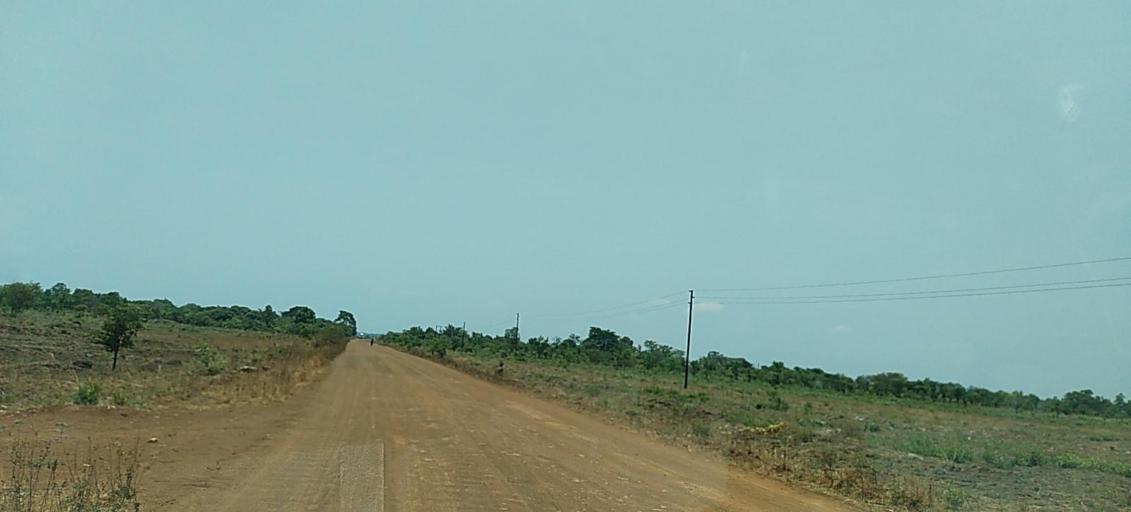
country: ZM
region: Copperbelt
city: Mpongwe
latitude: -13.6796
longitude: 27.8577
